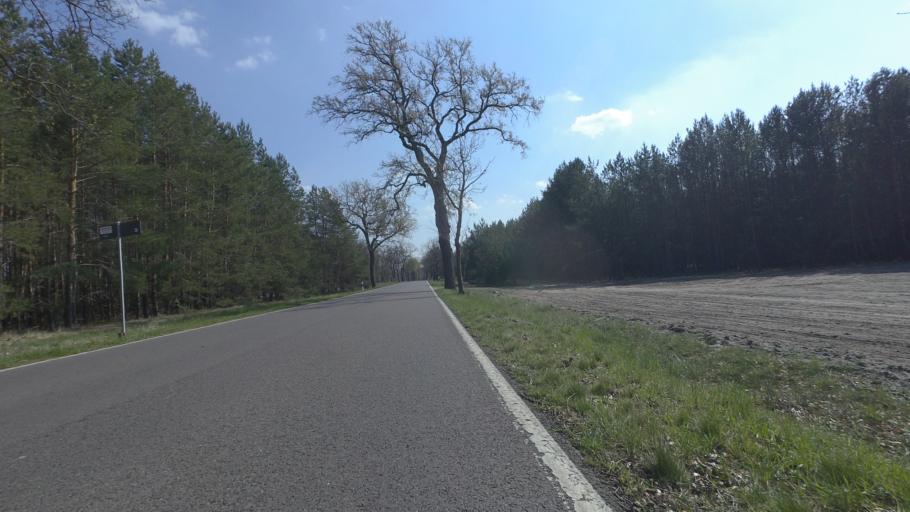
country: DE
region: Brandenburg
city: Mittenwalde
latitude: 52.2189
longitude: 13.5478
